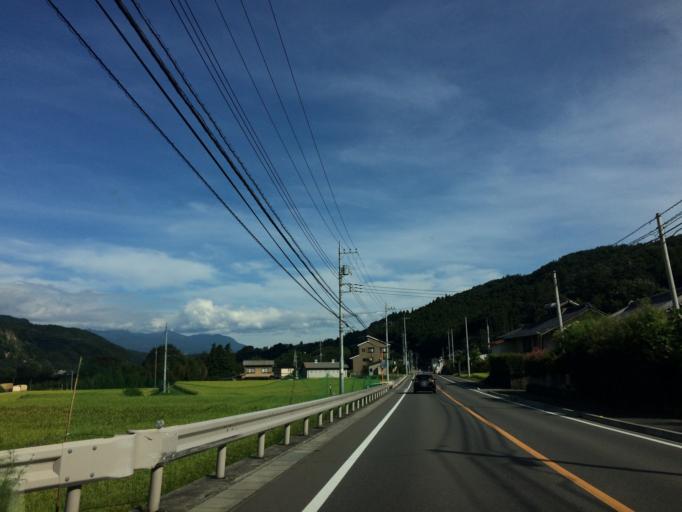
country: JP
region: Gunma
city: Nakanojomachi
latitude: 36.5522
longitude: 138.9046
